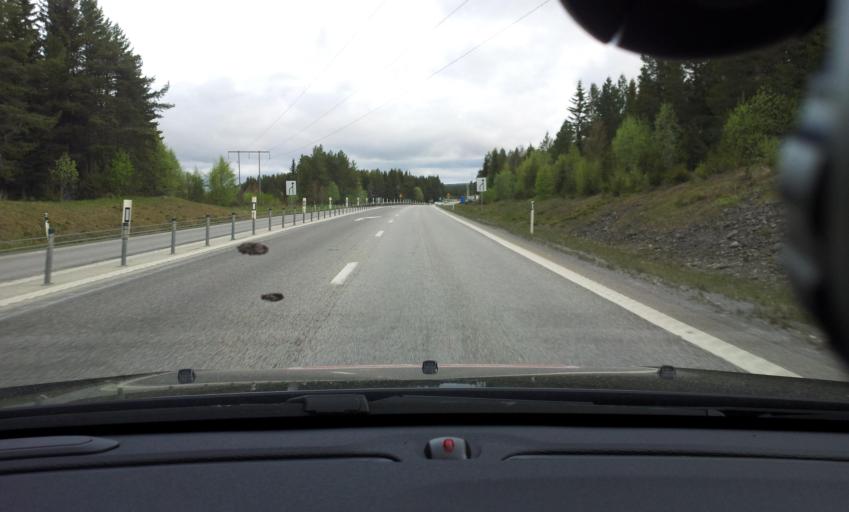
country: SE
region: Jaemtland
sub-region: OEstersunds Kommun
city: Brunflo
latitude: 63.1218
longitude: 14.7955
